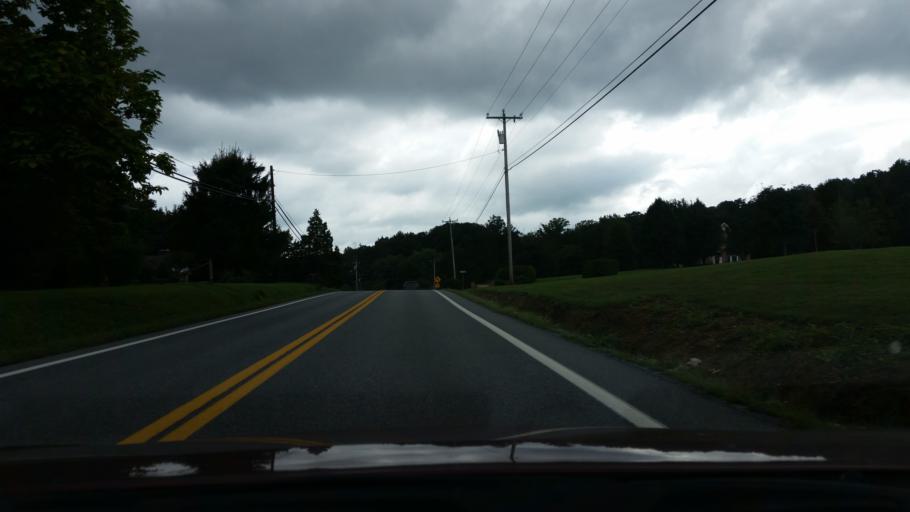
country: US
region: West Virginia
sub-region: Berkeley County
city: Martinsburg
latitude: 39.5676
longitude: -78.0384
